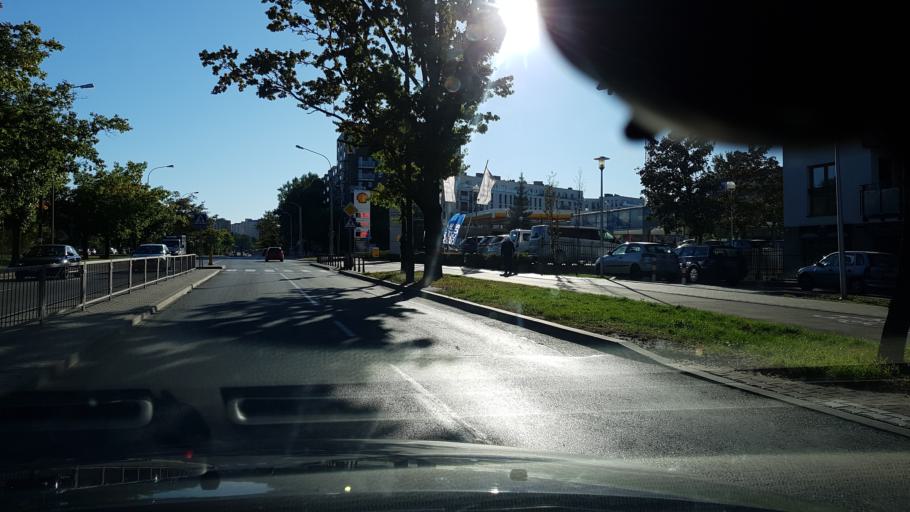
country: PL
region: Masovian Voivodeship
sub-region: Warszawa
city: Bielany
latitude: 52.2853
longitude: 20.9292
